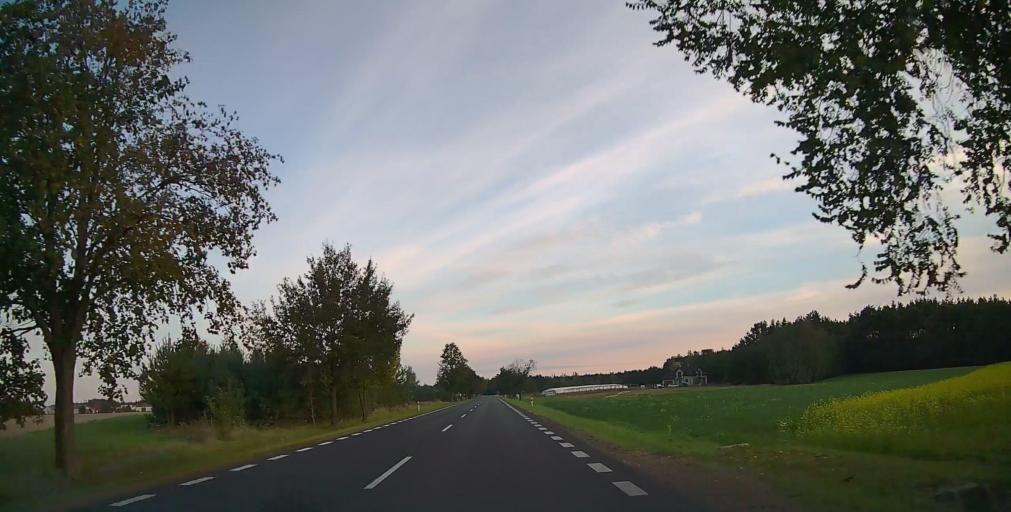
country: PL
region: Masovian Voivodeship
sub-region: Powiat kozienicki
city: Ryczywol
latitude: 51.7149
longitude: 21.3991
